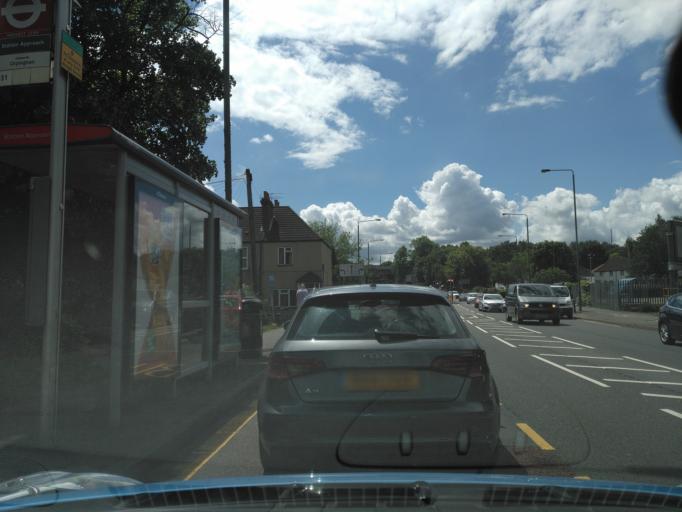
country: GB
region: England
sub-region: Greater London
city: Orpington
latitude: 51.3972
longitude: 0.1129
